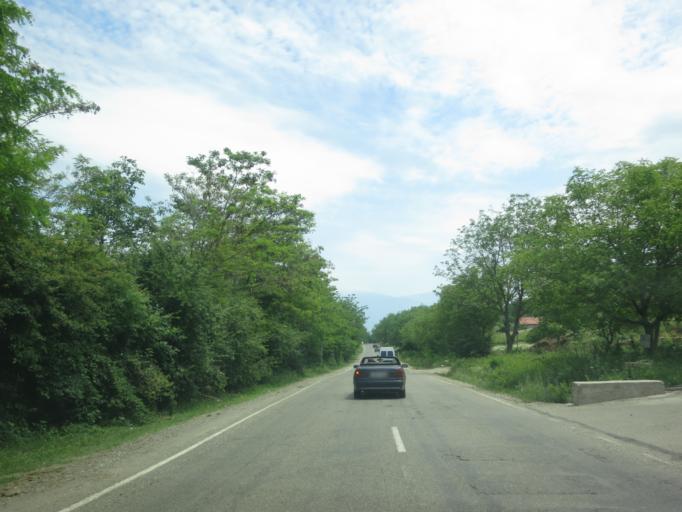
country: GE
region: Kakheti
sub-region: Telavi
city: Telavi
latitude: 41.9246
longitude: 45.4076
